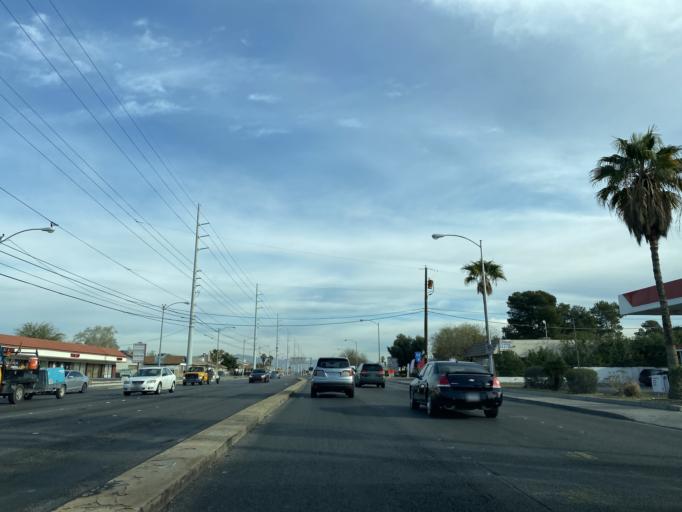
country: US
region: Nevada
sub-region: Clark County
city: Paradise
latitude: 36.0864
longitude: -115.1187
